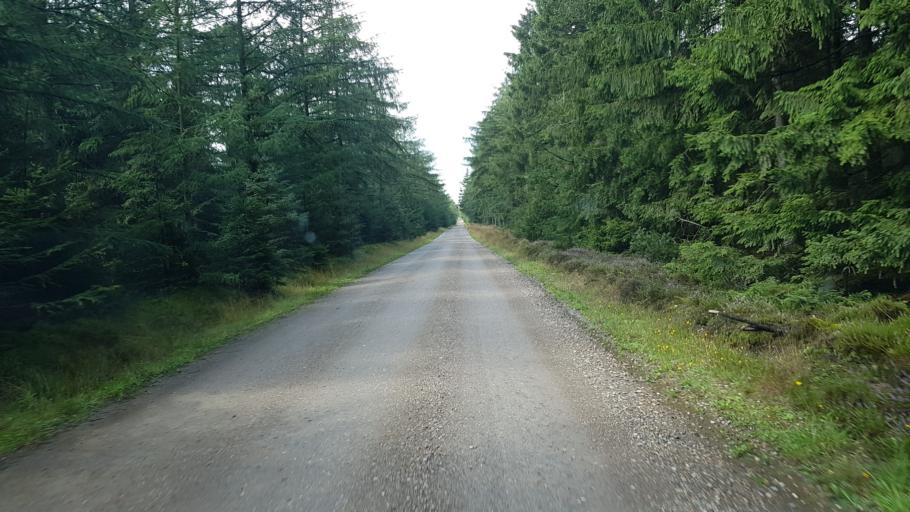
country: DK
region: South Denmark
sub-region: Vejen Kommune
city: Holsted
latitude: 55.5954
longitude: 8.8974
